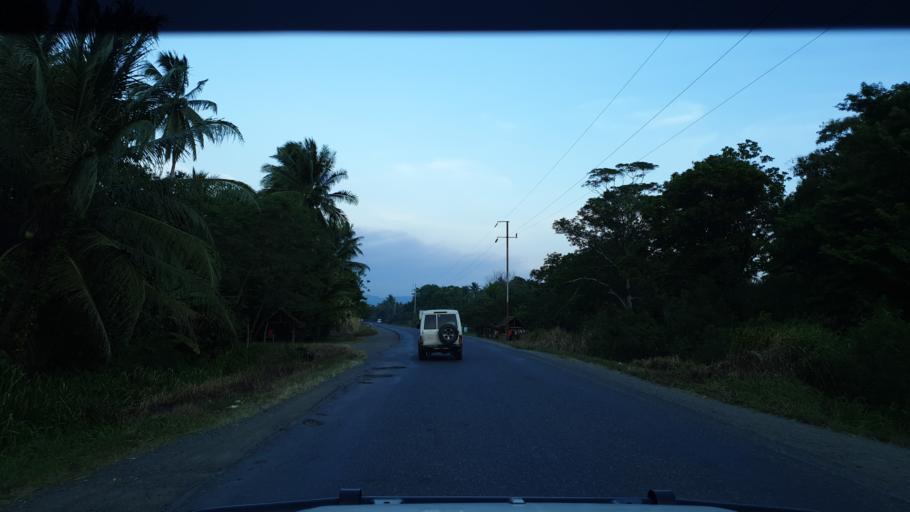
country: PG
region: Morobe
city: Lae
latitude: -6.5976
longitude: 146.7994
